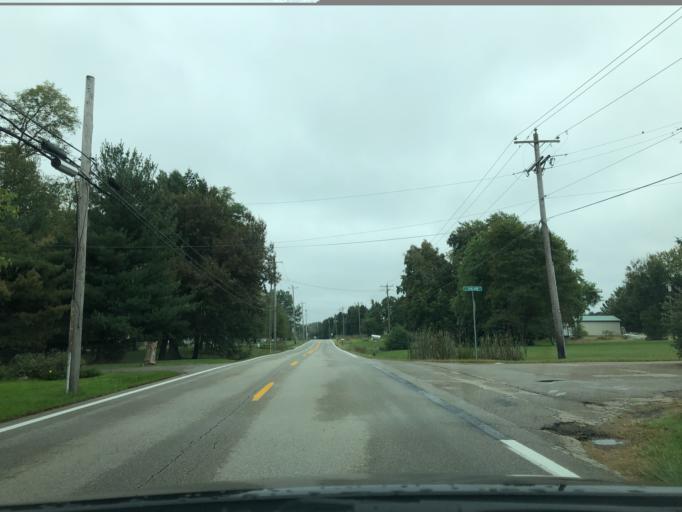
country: US
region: Ohio
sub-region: Hamilton County
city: Loveland
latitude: 39.2552
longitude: -84.2348
